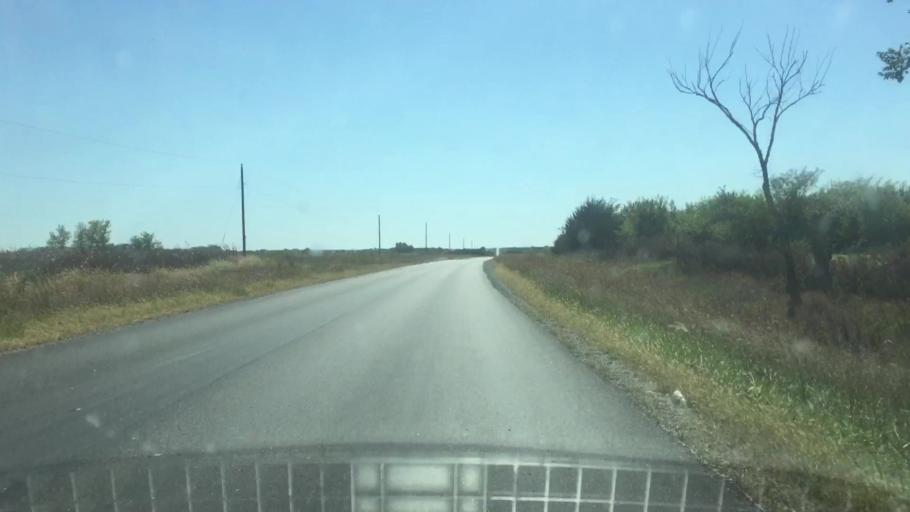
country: US
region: Kansas
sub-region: Marshall County
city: Marysville
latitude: 39.9512
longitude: -96.6008
